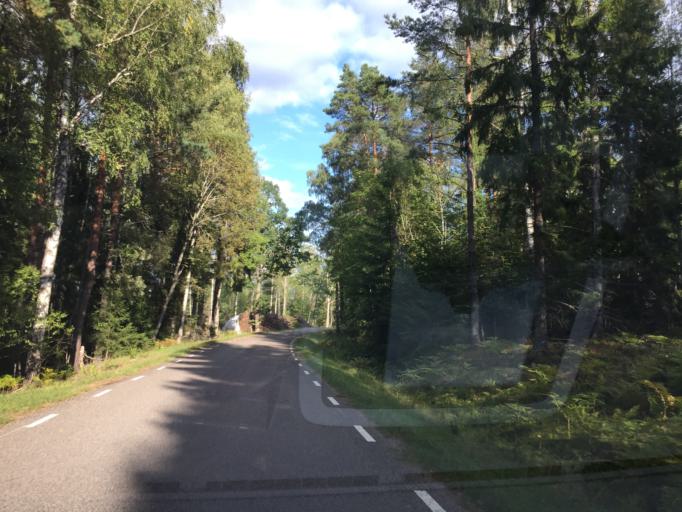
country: SE
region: Soedermanland
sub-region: Vingakers Kommun
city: Vingaker
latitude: 59.0081
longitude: 15.7280
